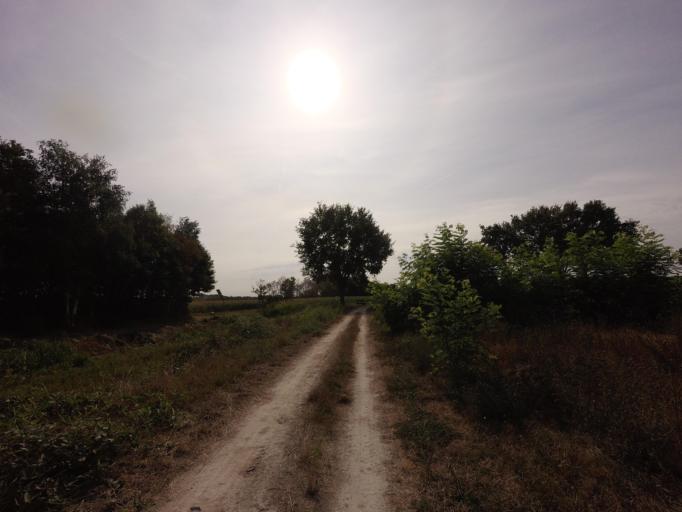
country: NL
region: North Brabant
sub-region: Gemeente Sint Anthonis
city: Sint Anthonis
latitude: 51.5765
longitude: 5.8477
